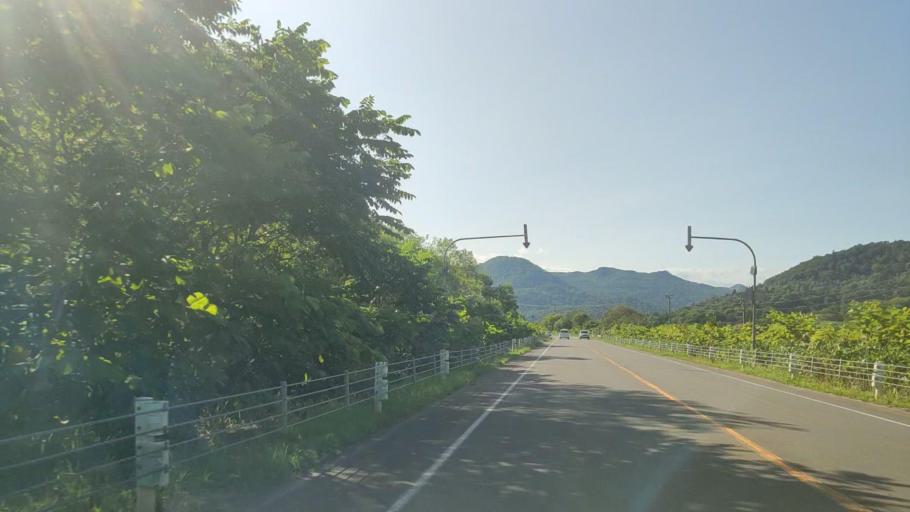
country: JP
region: Hokkaido
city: Nayoro
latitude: 44.7293
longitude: 142.2119
